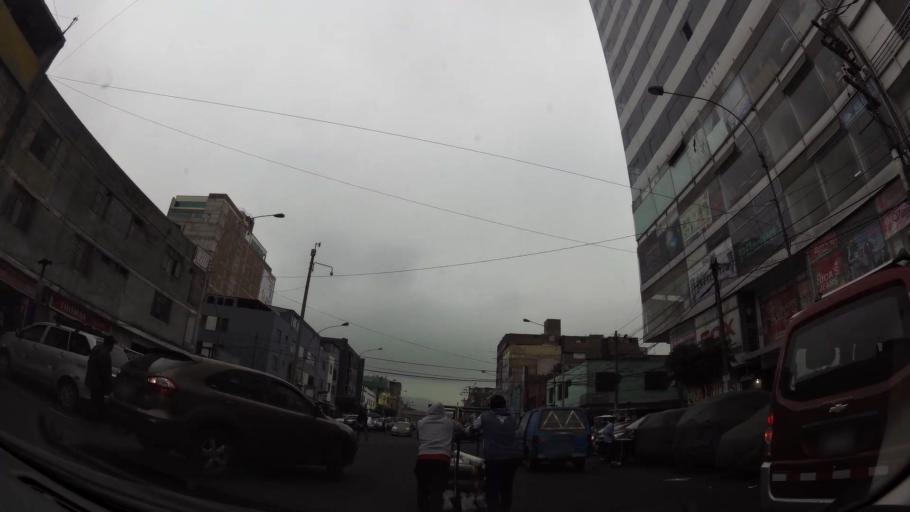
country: PE
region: Lima
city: Lima
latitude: -12.0627
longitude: -77.0150
